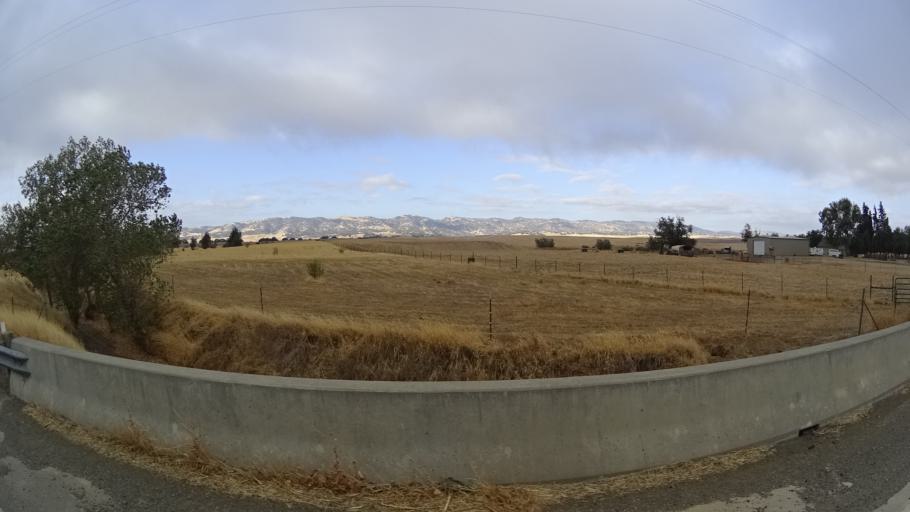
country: US
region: California
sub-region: Yolo County
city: Dunnigan
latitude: 38.8020
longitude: -122.0435
